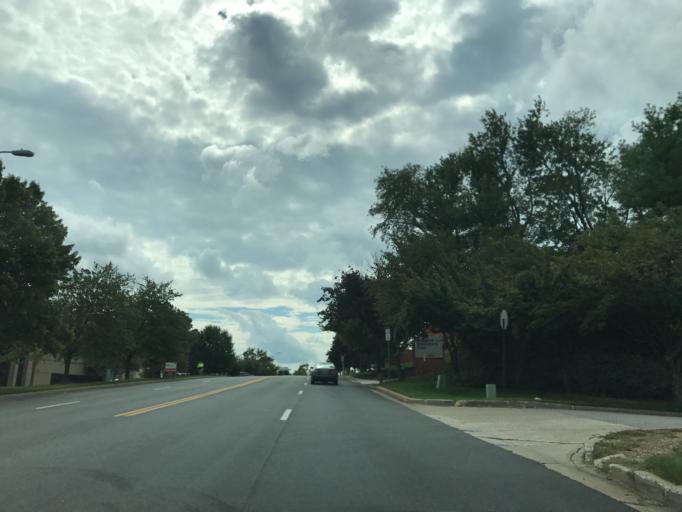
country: US
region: Maryland
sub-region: Baltimore County
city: Woodlawn
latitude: 39.3294
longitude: -76.7520
